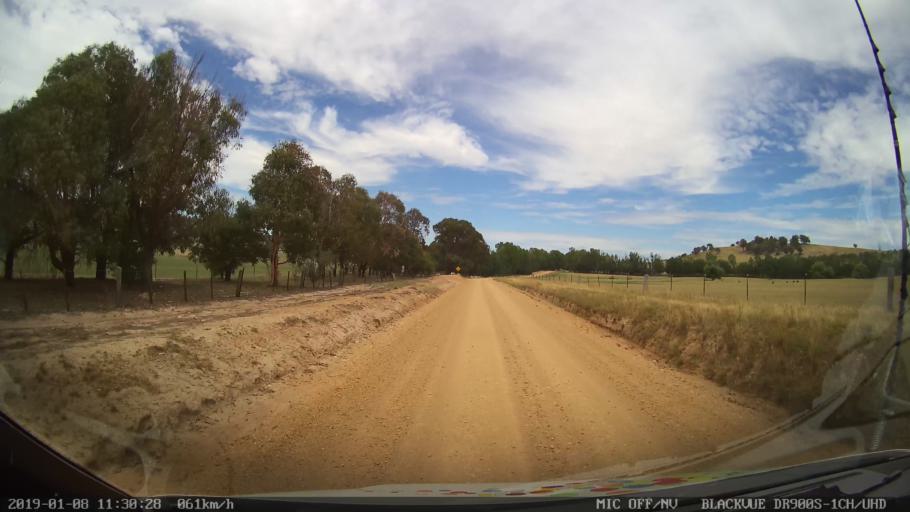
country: AU
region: New South Wales
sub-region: Guyra
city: Guyra
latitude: -30.3083
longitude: 151.5438
